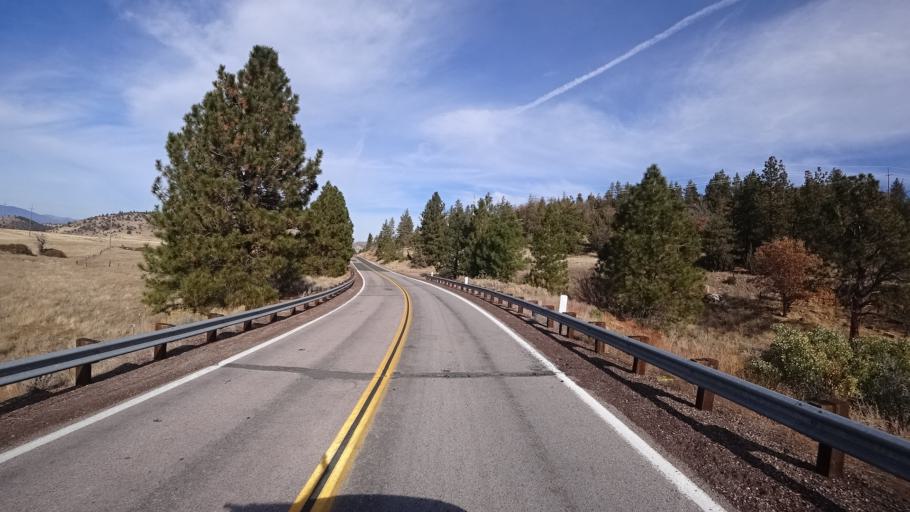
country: US
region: California
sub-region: Siskiyou County
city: Weed
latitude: 41.4686
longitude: -122.4140
